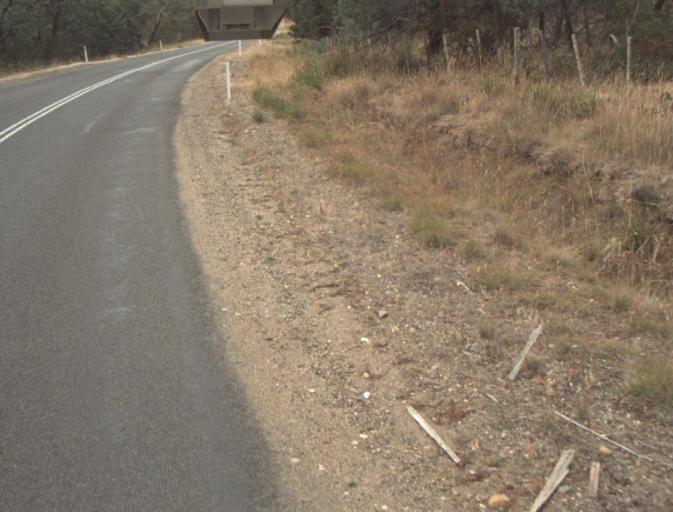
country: AU
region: Tasmania
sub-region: Northern Midlands
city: Evandale
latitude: -41.5120
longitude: 147.3405
